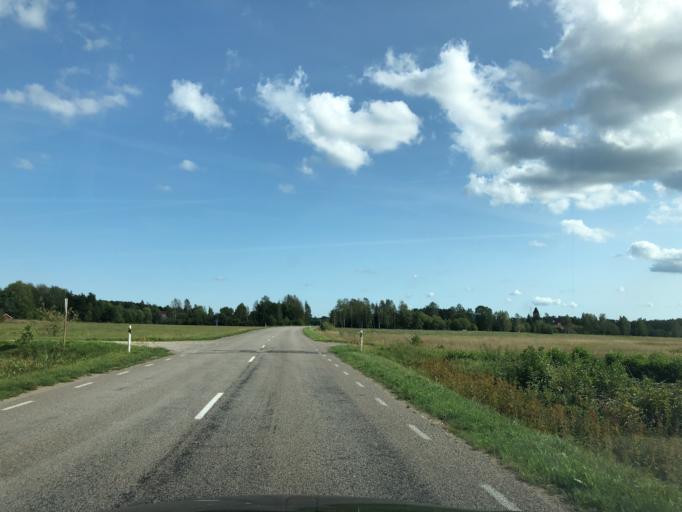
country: EE
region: Hiiumaa
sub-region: Kaerdla linn
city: Kardla
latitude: 58.7167
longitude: 22.5705
